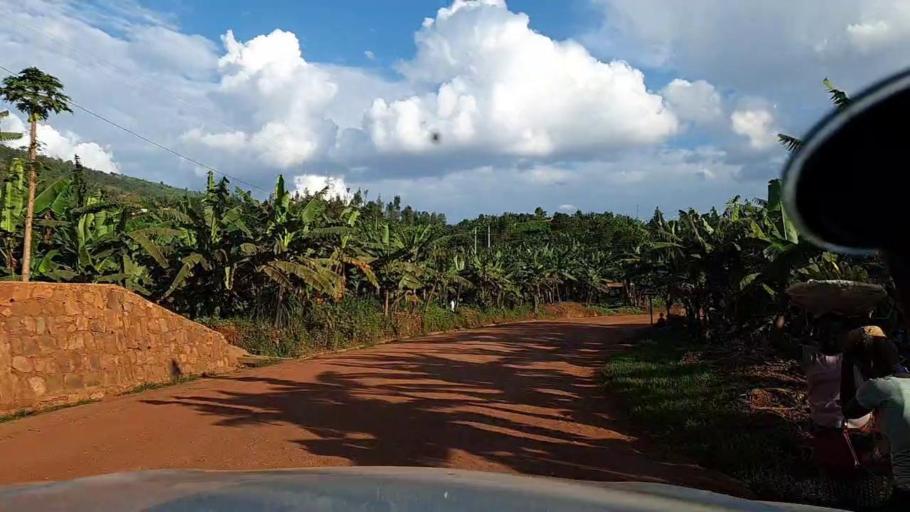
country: RW
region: Kigali
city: Kigali
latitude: -1.9280
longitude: 29.9923
